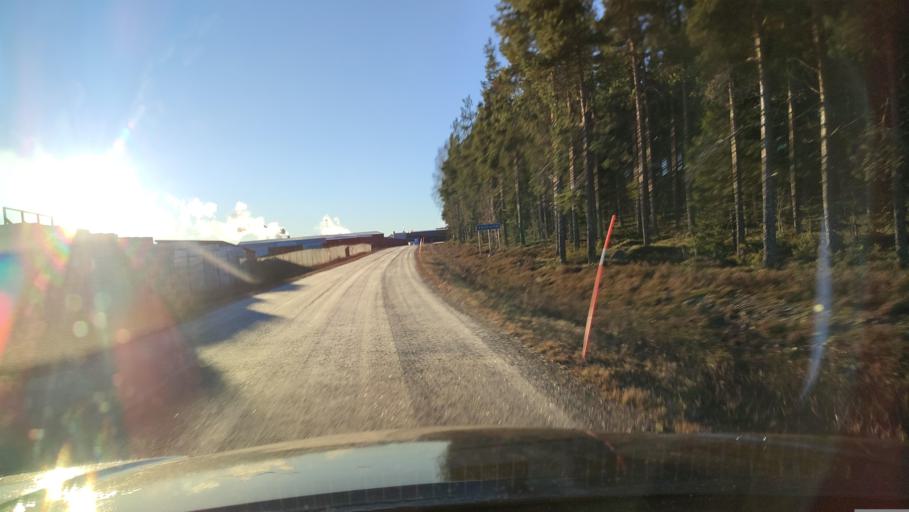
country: SE
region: Vaesterbotten
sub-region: Skelleftea Kommun
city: Viken
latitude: 64.7062
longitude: 20.9056
